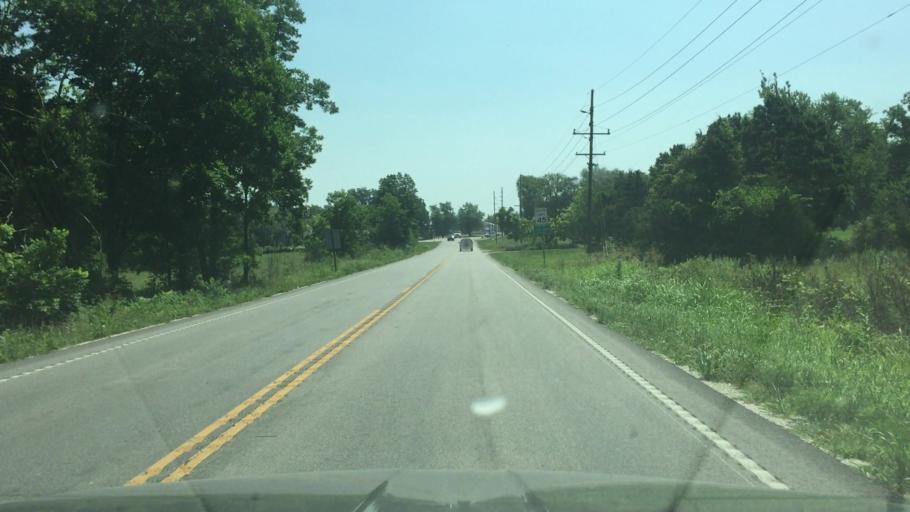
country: US
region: Missouri
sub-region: Miller County
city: Eldon
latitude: 38.3813
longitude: -92.6779
